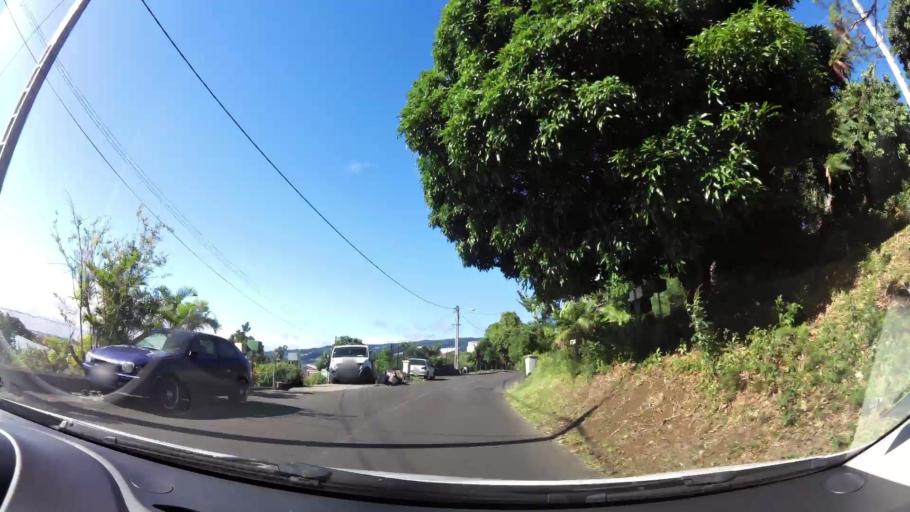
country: RE
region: Reunion
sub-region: Reunion
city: Saint-Denis
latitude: -20.9184
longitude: 55.4839
